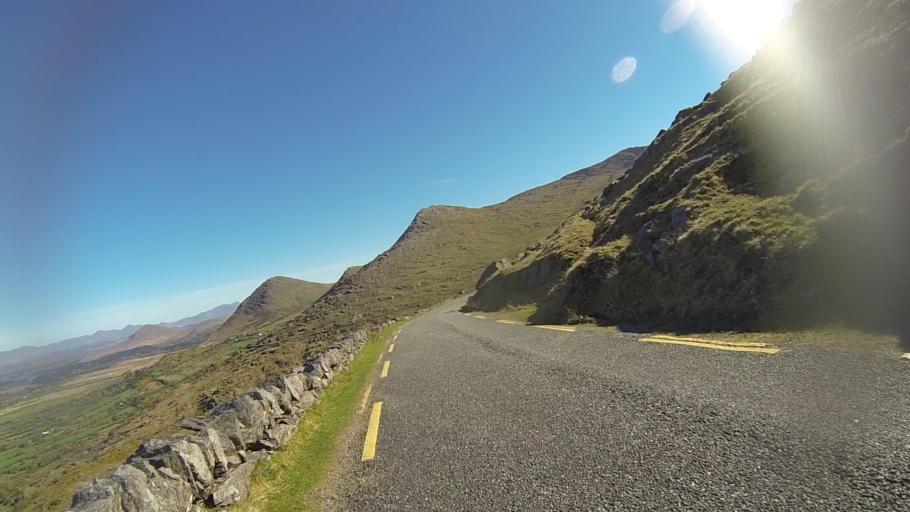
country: IE
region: Munster
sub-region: Ciarrai
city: Kenmare
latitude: 51.7261
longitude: -9.7580
